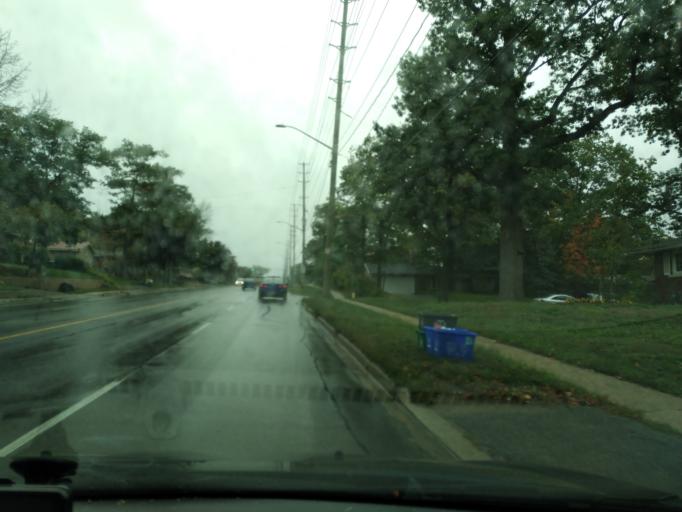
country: CA
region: Ontario
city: Barrie
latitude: 44.3922
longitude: -79.7135
